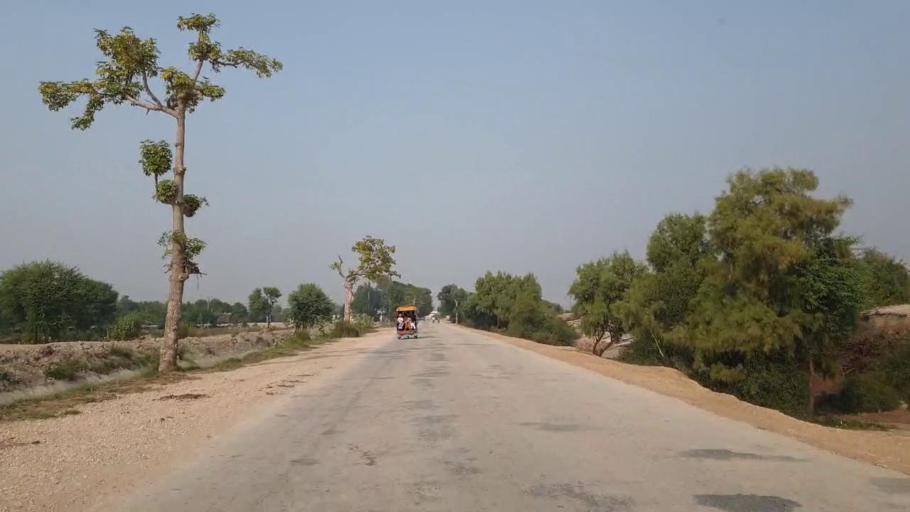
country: PK
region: Sindh
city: Bhan
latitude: 26.5845
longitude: 67.7290
